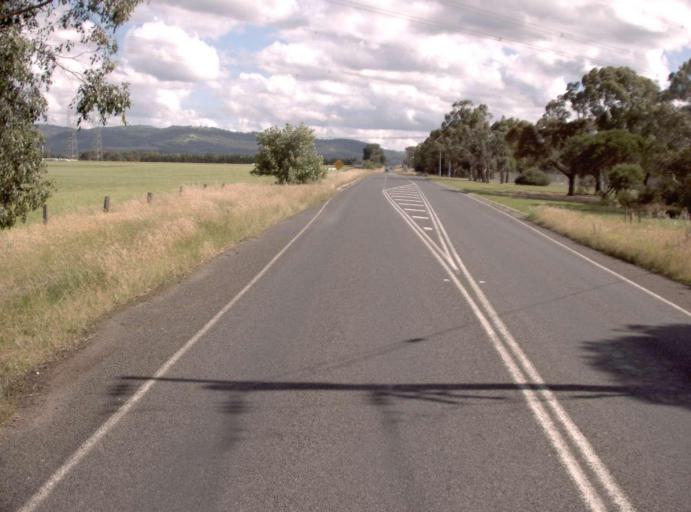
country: AU
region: Victoria
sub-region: Latrobe
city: Morwell
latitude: -38.2781
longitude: 146.4321
